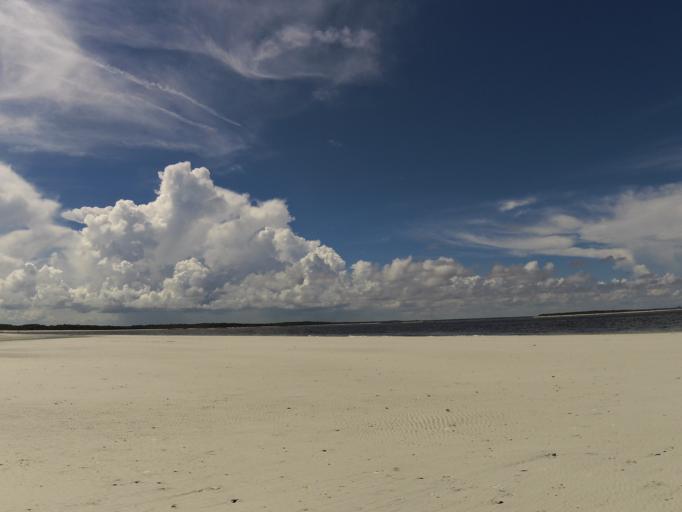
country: US
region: Florida
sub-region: Duval County
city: Atlantic Beach
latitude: 30.4885
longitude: -81.4155
